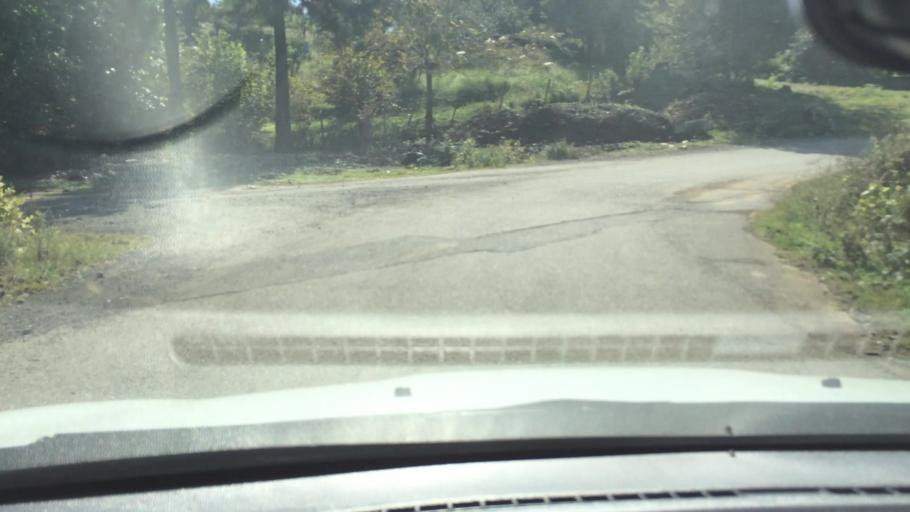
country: GE
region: Ajaria
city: Kobuleti
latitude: 41.8107
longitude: 41.8251
